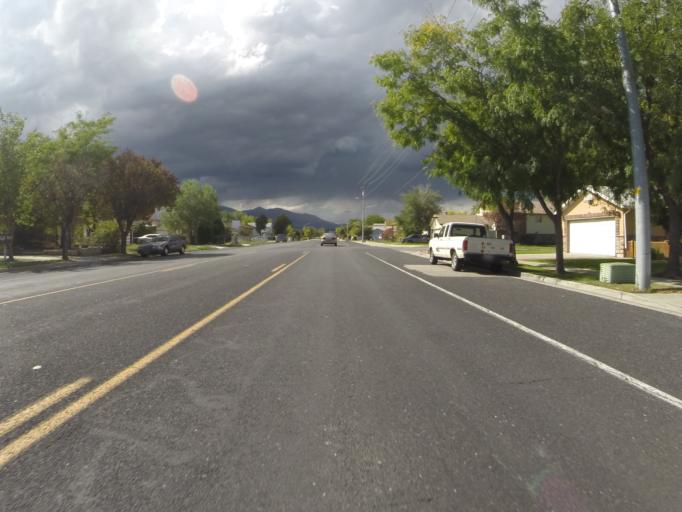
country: US
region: Utah
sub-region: Salt Lake County
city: West Valley City
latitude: 40.7039
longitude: -112.0022
